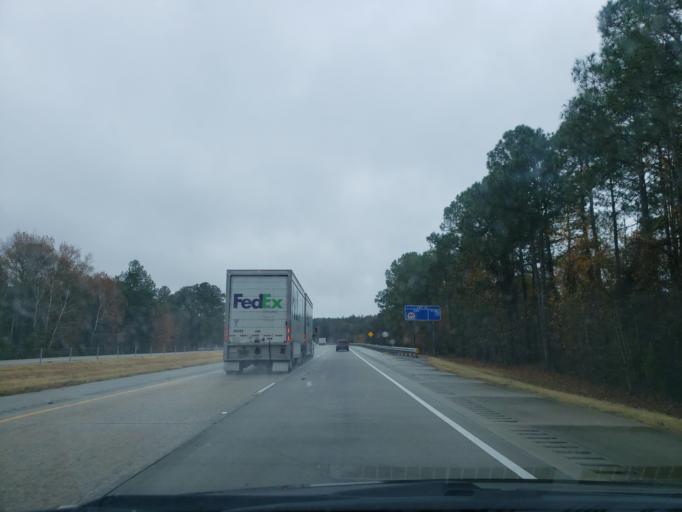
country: US
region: Georgia
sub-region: Treutlen County
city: Soperton
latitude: 32.4351
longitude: -82.7046
